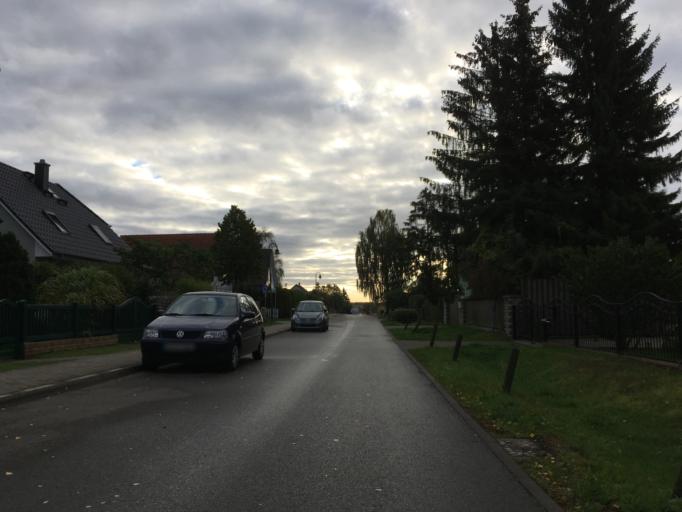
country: DE
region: Berlin
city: Falkenberg
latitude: 52.5907
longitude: 13.5376
